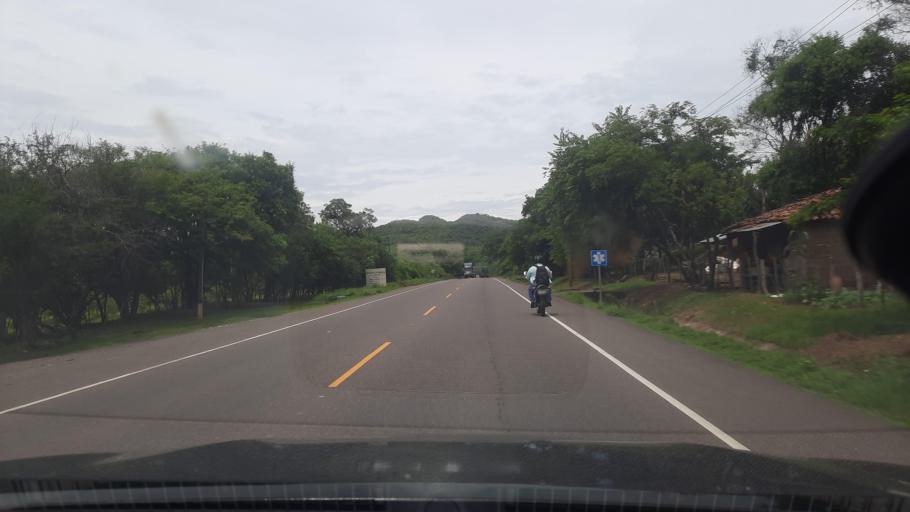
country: HN
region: Valle
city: Langue
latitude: 13.5952
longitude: -87.7043
